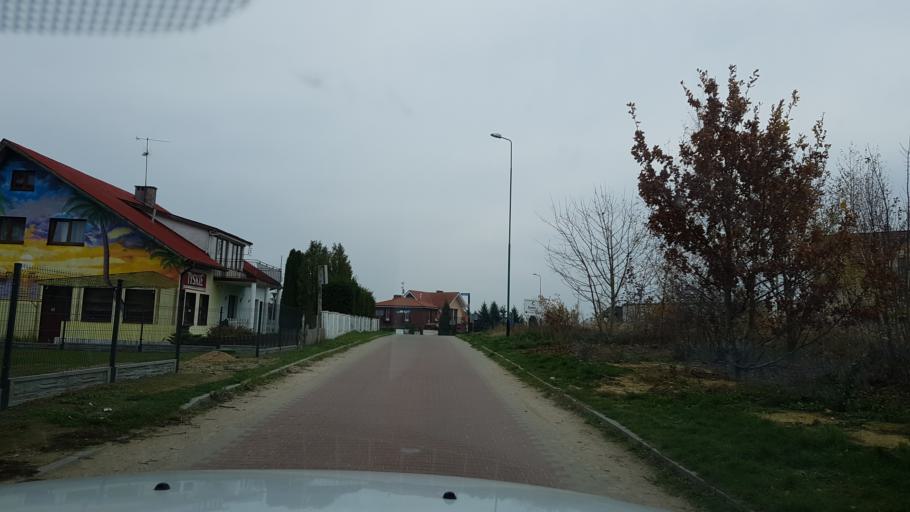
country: PL
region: West Pomeranian Voivodeship
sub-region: Powiat gryficki
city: Rewal
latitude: 54.0840
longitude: 15.0268
